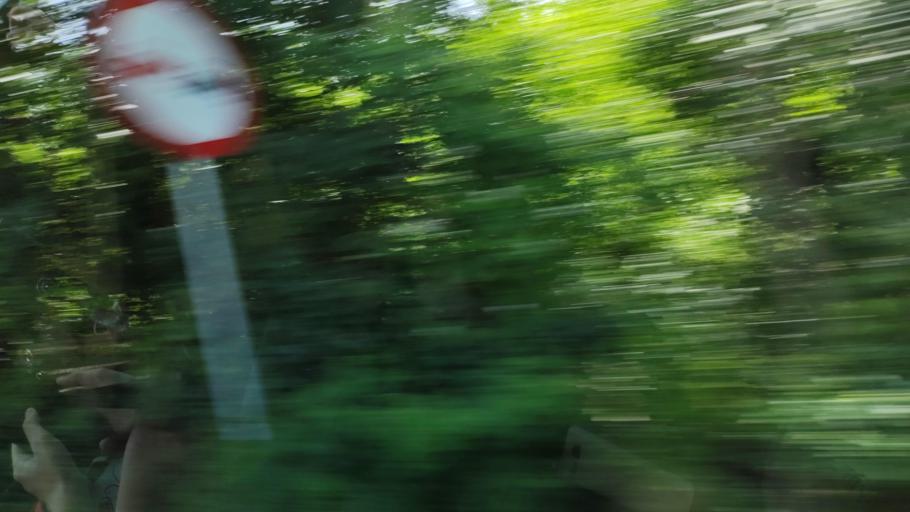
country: RO
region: Mehedinti
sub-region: Comuna Eselnita
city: Eselnita
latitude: 44.7217
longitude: 22.3633
